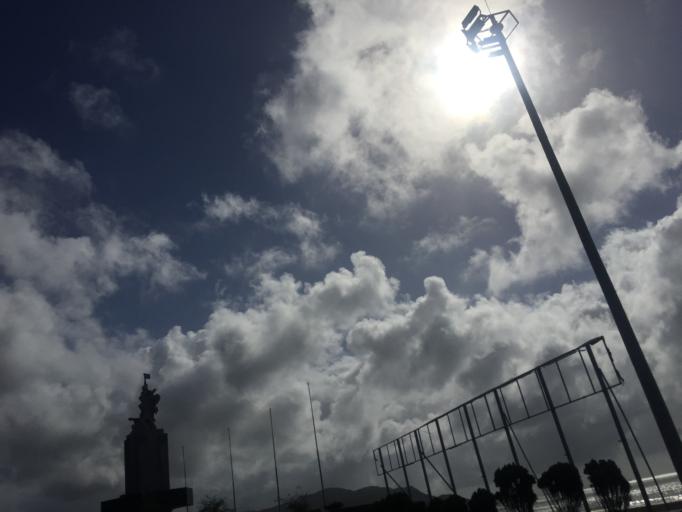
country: VN
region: Binh Dinh
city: Qui Nhon
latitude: 13.7697
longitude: 109.2341
